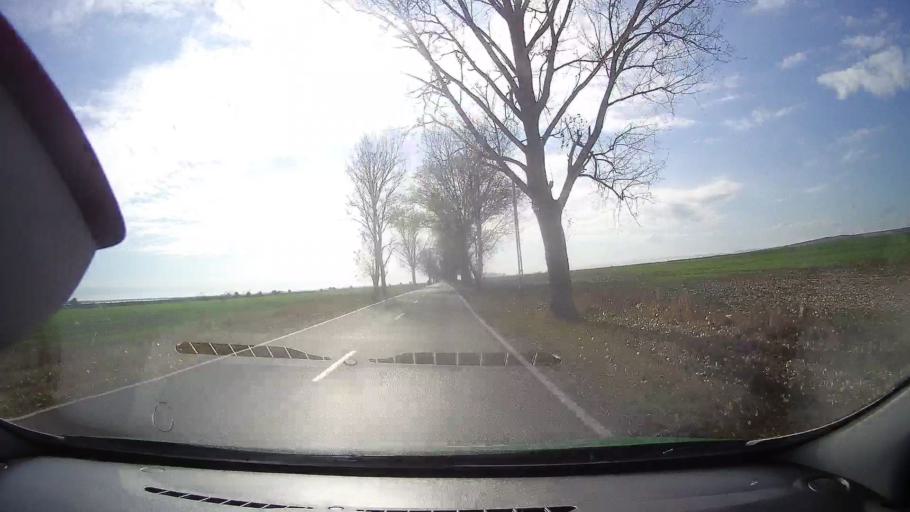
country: RO
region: Tulcea
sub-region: Comuna Valea Nucarilor
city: Agighiol
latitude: 45.0119
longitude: 28.8841
